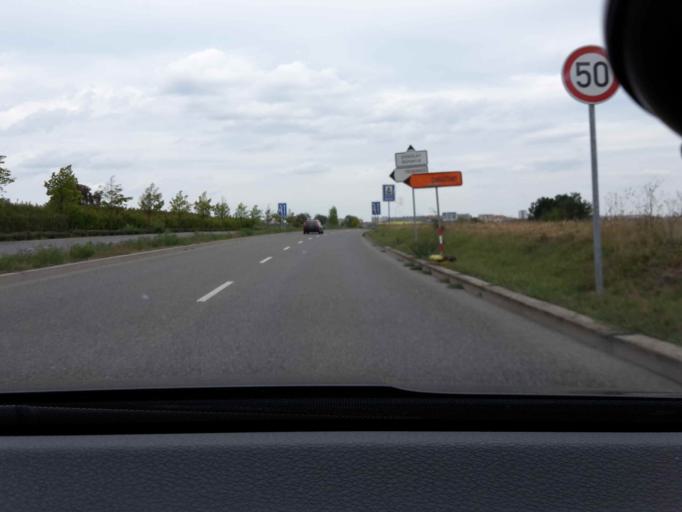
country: CZ
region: Central Bohemia
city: Hostivice
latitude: 50.0362
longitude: 14.2901
